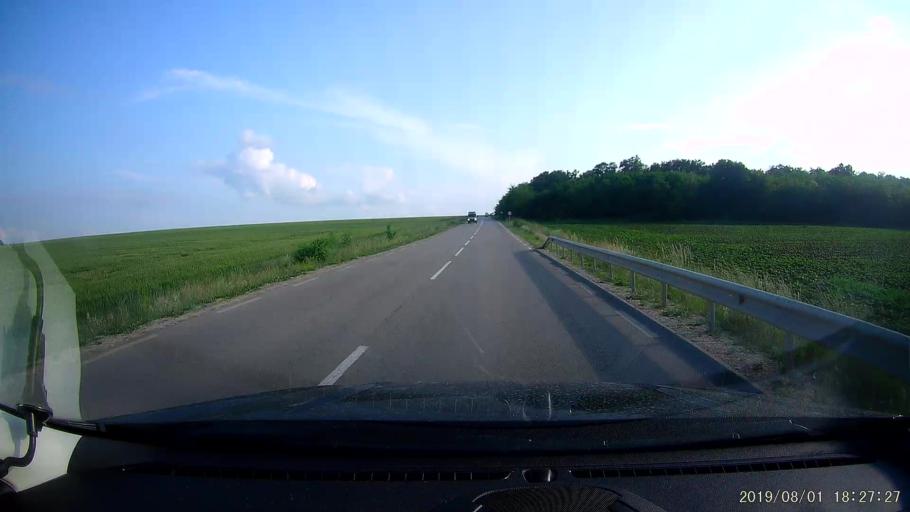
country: BG
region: Shumen
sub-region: Obshtina Venets
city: Venets
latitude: 43.5868
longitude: 26.9822
